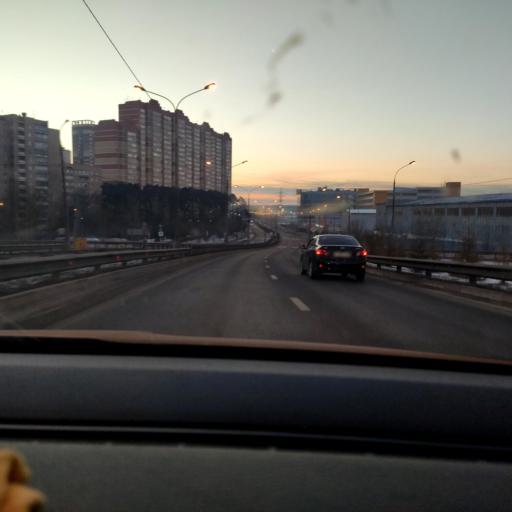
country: RU
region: Moskovskaya
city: Odintsovo
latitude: 55.6676
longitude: 37.2798
